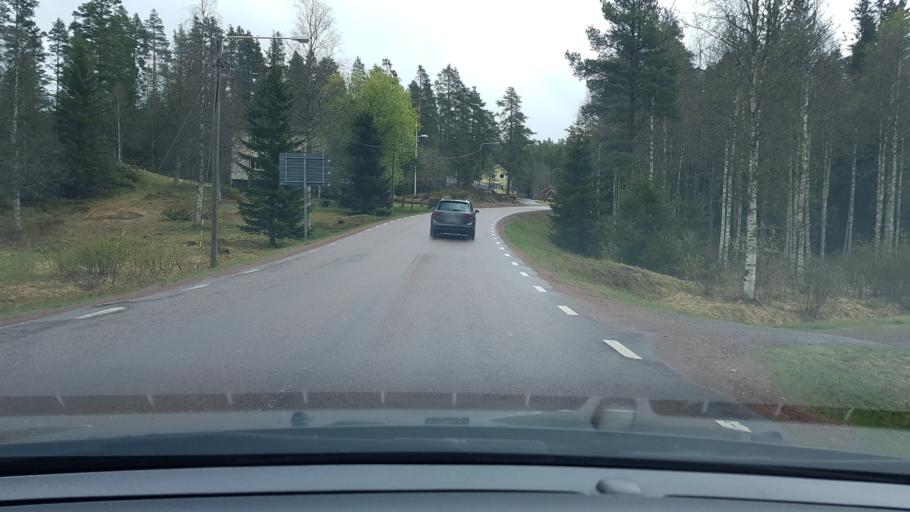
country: SE
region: Dalarna
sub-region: Malung-Saelens kommun
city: Malung
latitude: 61.0670
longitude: 13.3323
